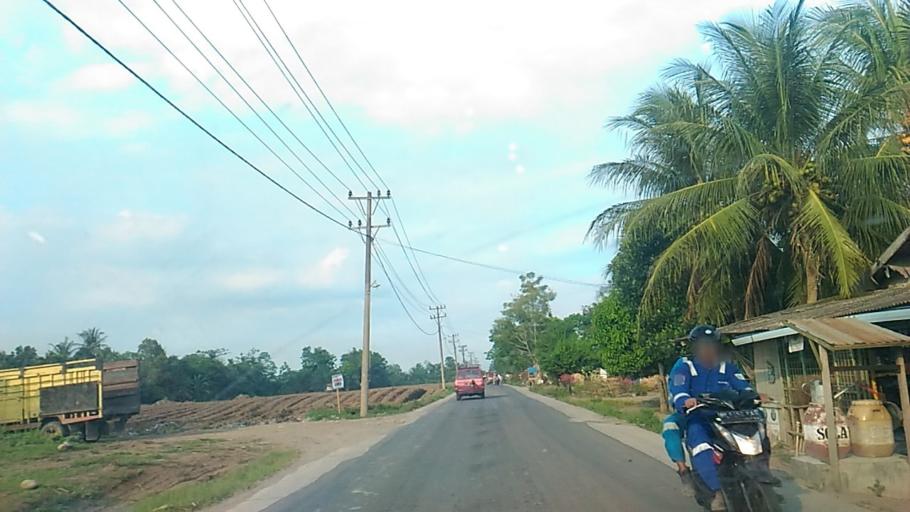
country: ID
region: North Sumatra
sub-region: Kabupaten Langkat
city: Stabat
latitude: 3.7034
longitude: 98.5462
